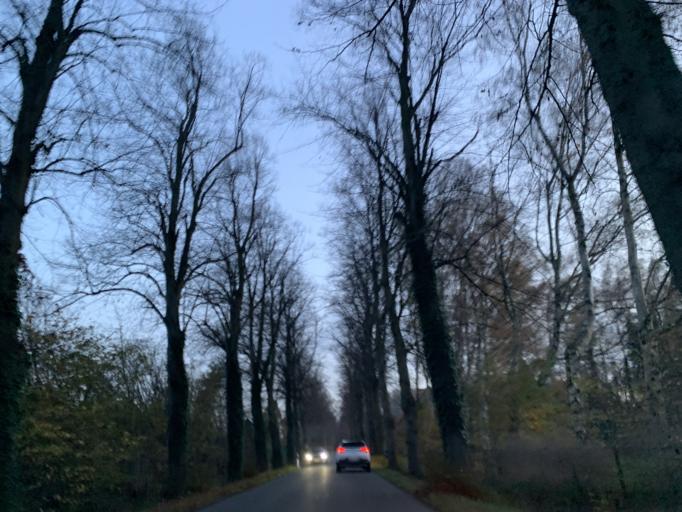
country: DE
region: North Rhine-Westphalia
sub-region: Regierungsbezirk Munster
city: Havixbeck
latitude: 51.9617
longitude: 7.5080
